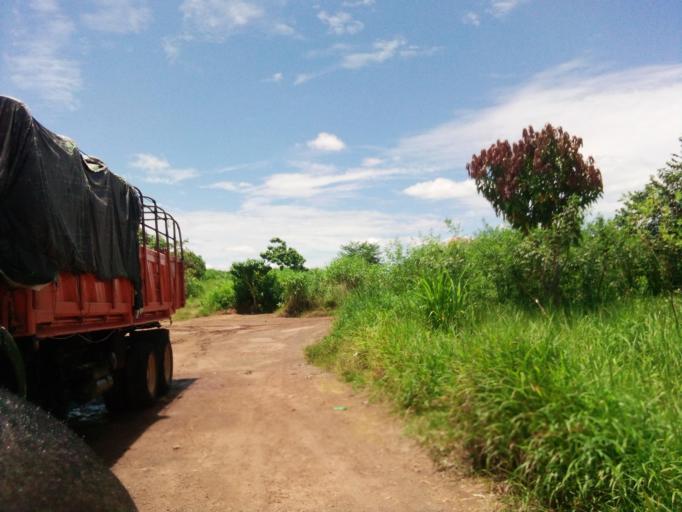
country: SL
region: Eastern Province
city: Koidu
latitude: 8.6423
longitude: -10.9277
